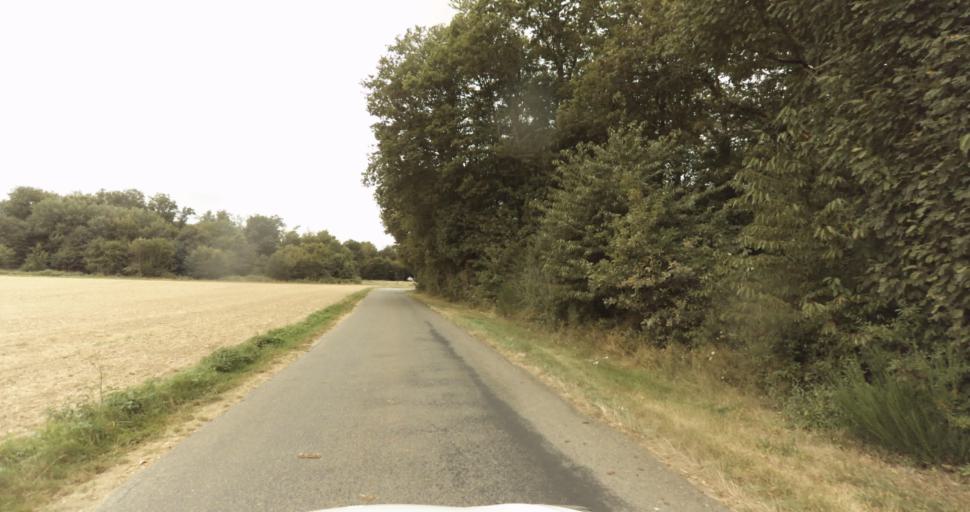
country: FR
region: Haute-Normandie
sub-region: Departement de l'Eure
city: La Madeleine-de-Nonancourt
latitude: 48.8195
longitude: 1.2242
